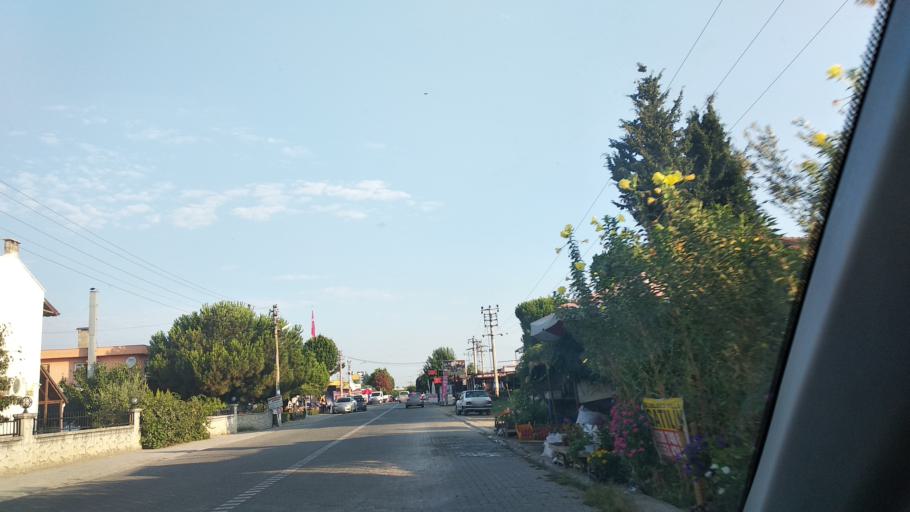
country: TR
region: Balikesir
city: Altinova
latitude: 39.1573
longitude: 26.8235
